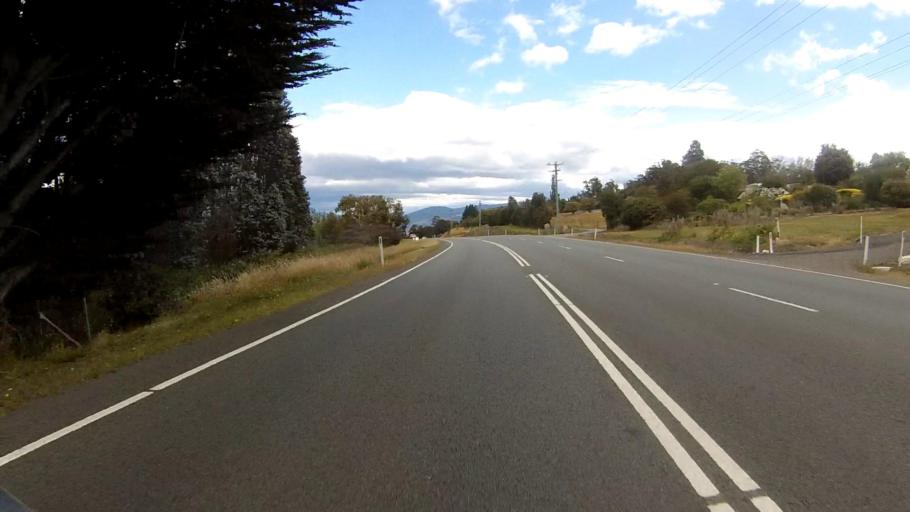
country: AU
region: Tasmania
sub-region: Huon Valley
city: Huonville
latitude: -42.9777
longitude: 147.1404
